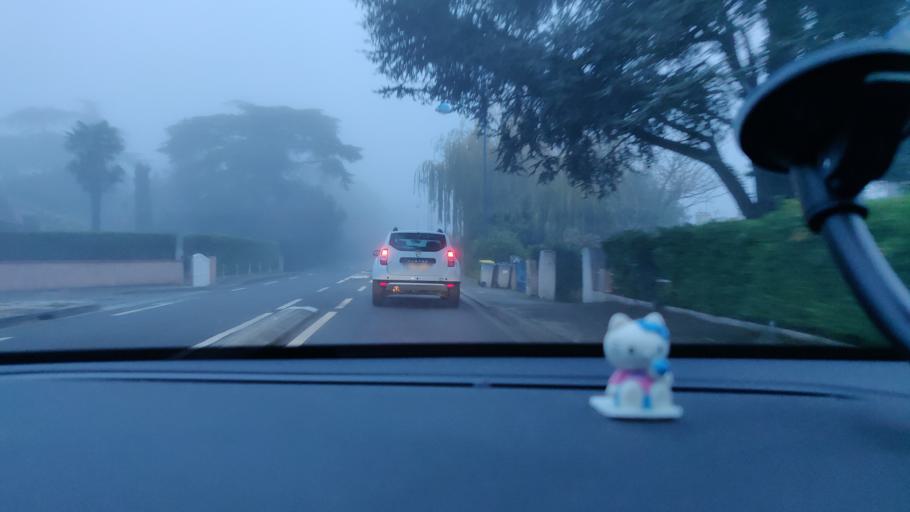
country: FR
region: Midi-Pyrenees
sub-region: Departement de la Haute-Garonne
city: Vieille-Toulouse
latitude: 43.5229
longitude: 1.4623
